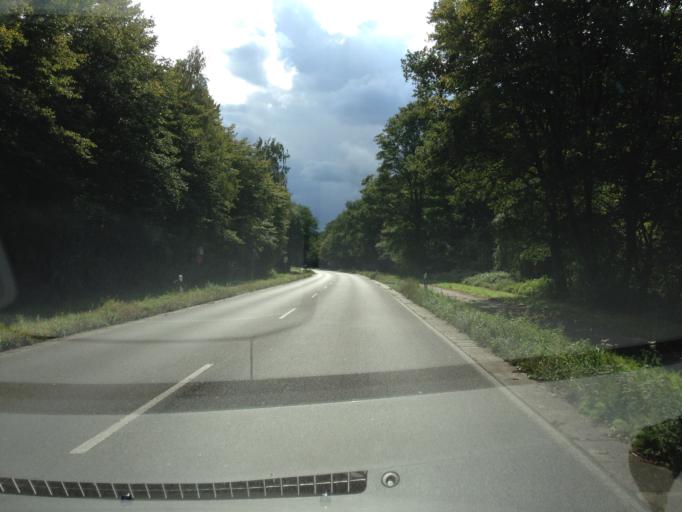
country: DE
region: North Rhine-Westphalia
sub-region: Regierungsbezirk Koln
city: Eil
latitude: 50.8957
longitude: 7.1015
